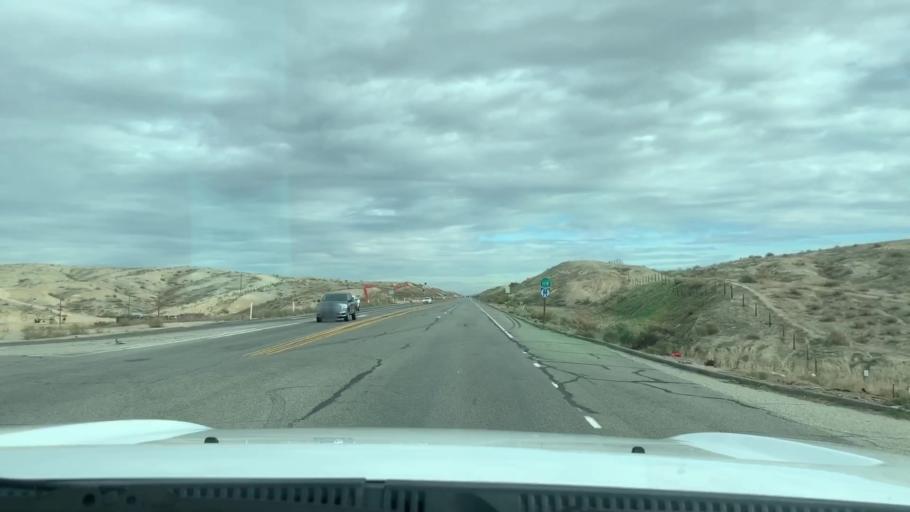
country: US
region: California
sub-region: Kern County
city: Ford City
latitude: 35.2391
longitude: -119.3593
